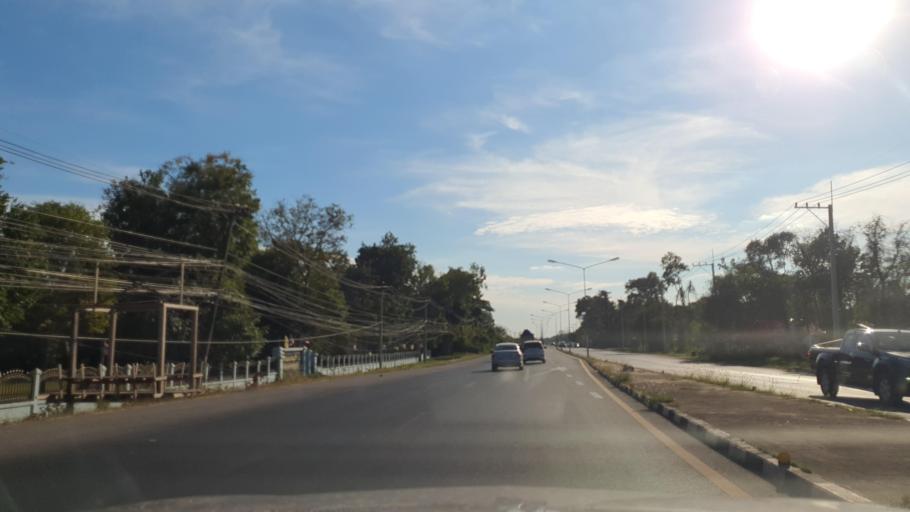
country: TH
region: Kalasin
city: Yang Talat
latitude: 16.3703
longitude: 103.3448
